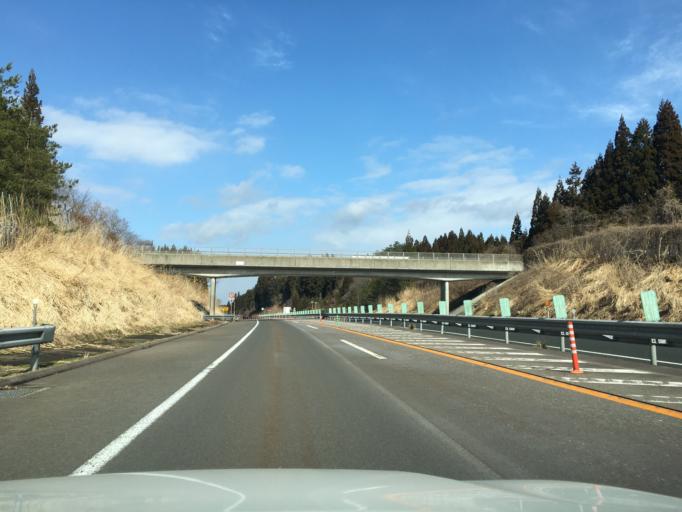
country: JP
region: Akita
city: Akita
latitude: 39.7283
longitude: 140.1800
